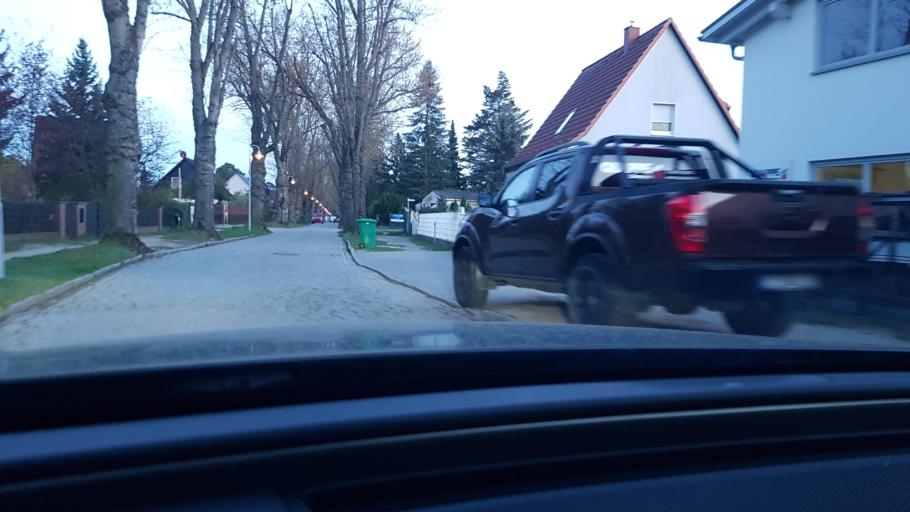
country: DE
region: Brandenburg
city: Rangsdorf
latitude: 52.3436
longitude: 13.4192
